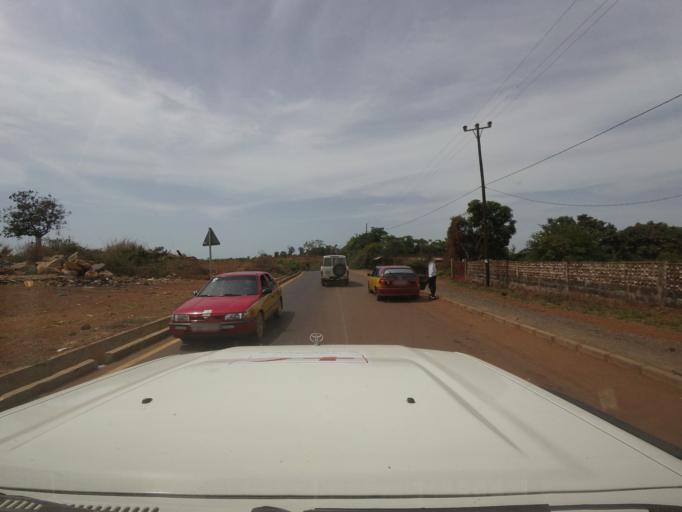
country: SL
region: Western Area
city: Freetown
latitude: 8.4629
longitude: -13.2185
